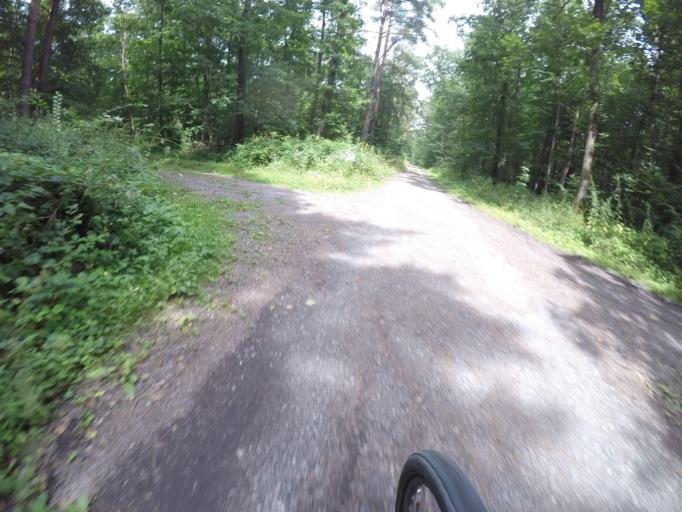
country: DE
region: Baden-Wuerttemberg
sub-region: Karlsruhe Region
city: Hambrucken
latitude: 49.2016
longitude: 8.5483
